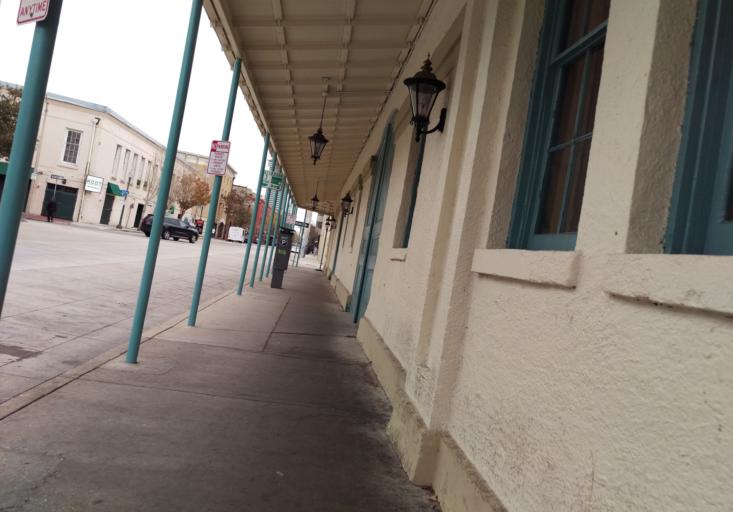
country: US
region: Louisiana
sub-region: Orleans Parish
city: New Orleans
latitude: 29.9443
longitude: -90.0647
